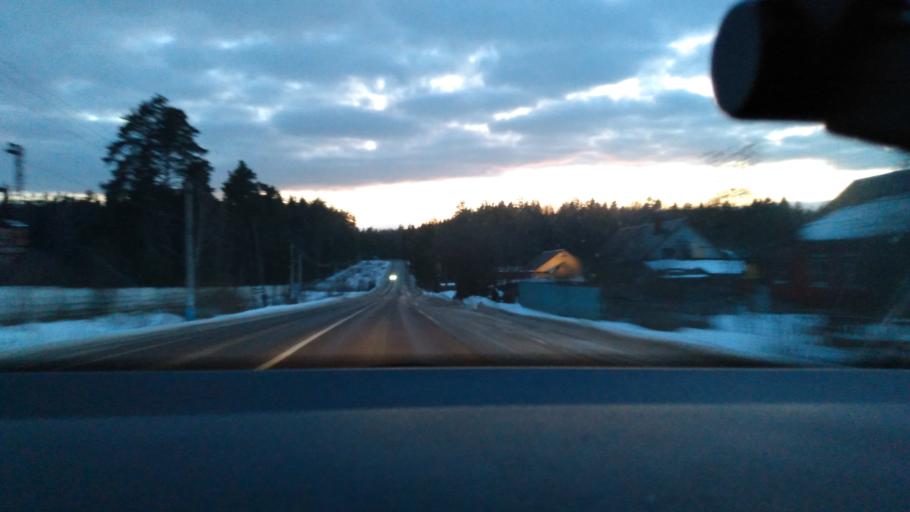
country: RU
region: Moskovskaya
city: Yegor'yevsk
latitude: 55.2725
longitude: 39.0784
